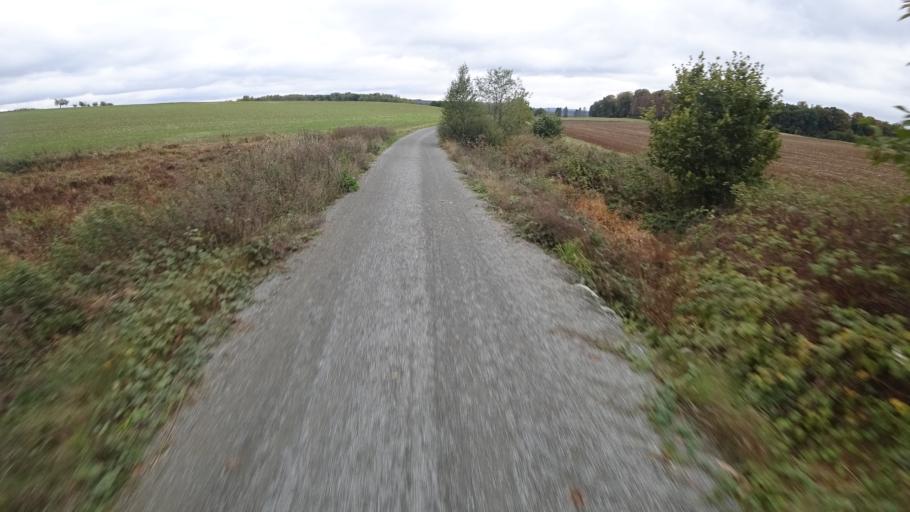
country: DE
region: Rheinland-Pfalz
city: Maxsain
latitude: 50.5577
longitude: 7.7795
